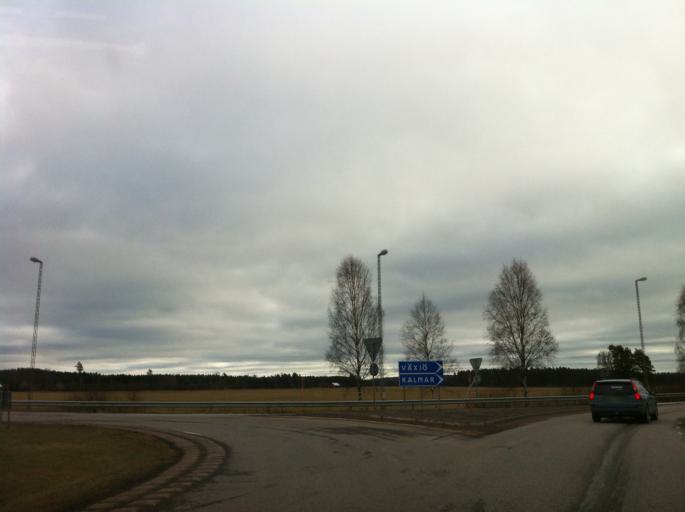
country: SE
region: Kalmar
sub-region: Vimmerby Kommun
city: Vimmerby
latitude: 57.6502
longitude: 15.8235
